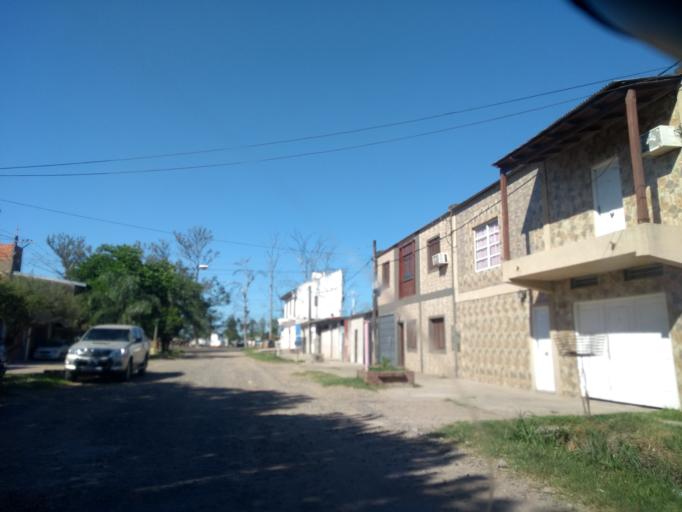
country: AR
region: Chaco
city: Resistencia
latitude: -27.4719
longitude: -58.9788
